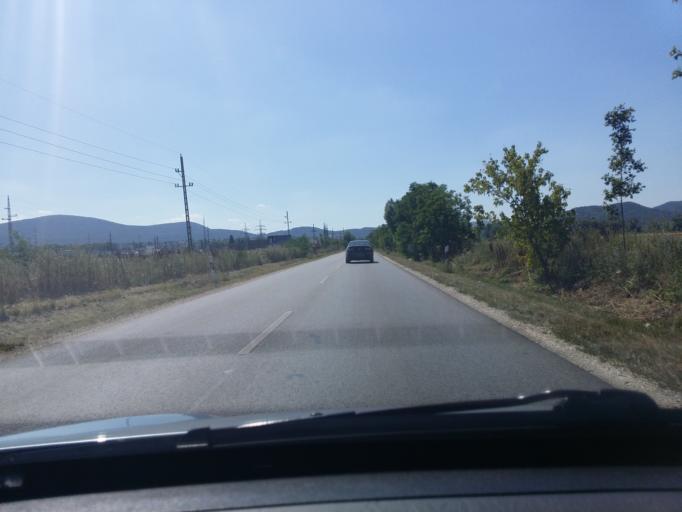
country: HU
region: Pest
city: Pomaz
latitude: 47.6456
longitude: 19.0553
